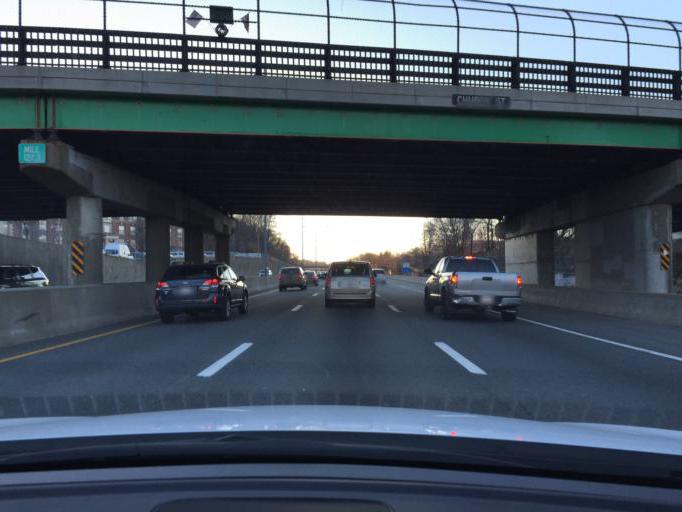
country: US
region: Massachusetts
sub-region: Middlesex County
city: Watertown
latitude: 42.3557
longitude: -71.1897
